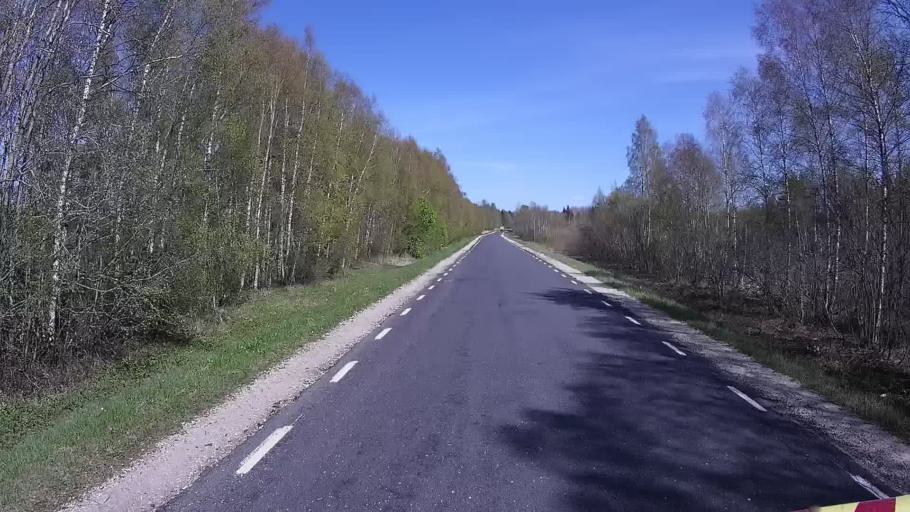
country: EE
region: Laeaene
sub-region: Ridala Parish
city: Uuemoisa
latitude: 59.0213
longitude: 23.8015
